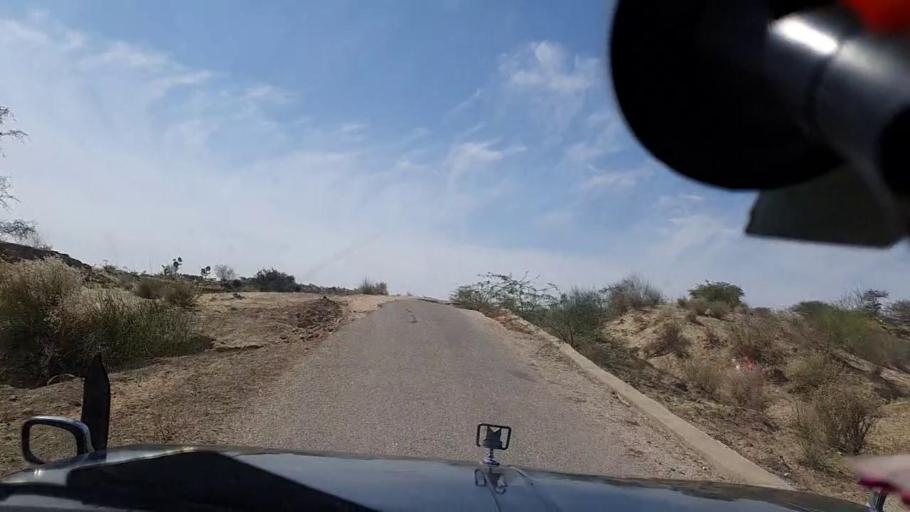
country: PK
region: Sindh
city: Diplo
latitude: 24.3899
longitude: 69.5889
